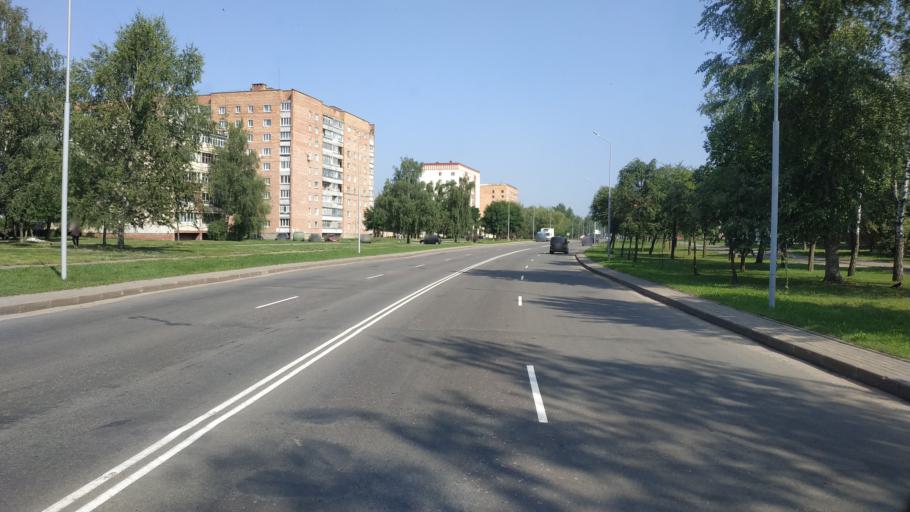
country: BY
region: Mogilev
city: Buynichy
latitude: 53.8676
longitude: 30.3143
